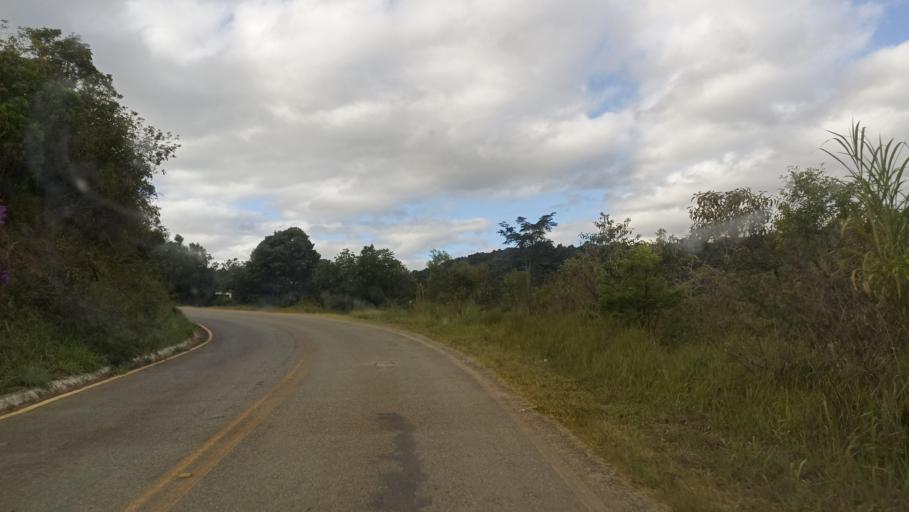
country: BR
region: Minas Gerais
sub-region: Tiradentes
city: Tiradentes
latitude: -21.0772
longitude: -44.0739
